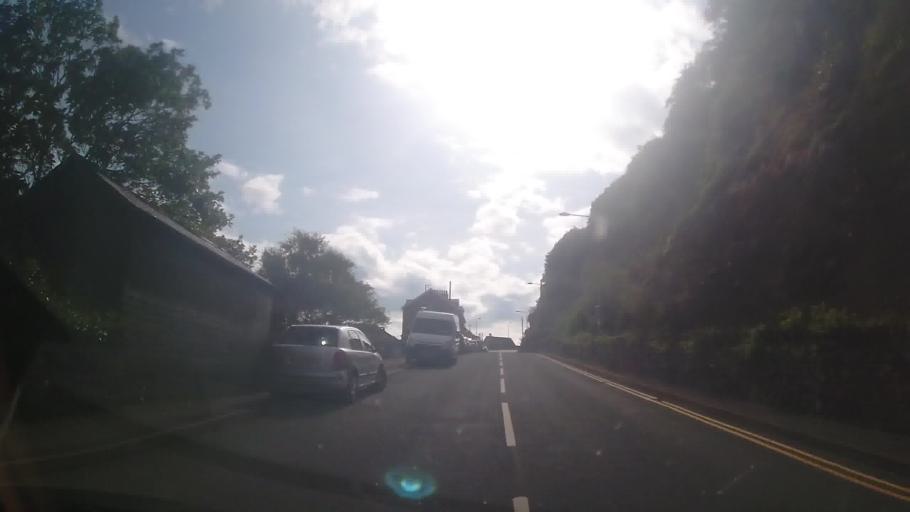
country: GB
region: Wales
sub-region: Gwynedd
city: Barmouth
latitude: 52.7212
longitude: -4.0421
